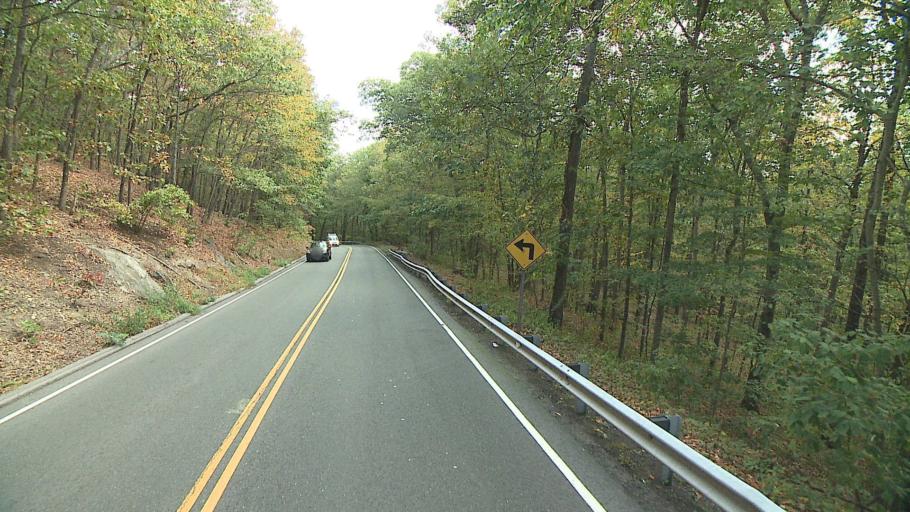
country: US
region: Connecticut
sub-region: New Haven County
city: Ansonia
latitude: 41.3548
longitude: -73.1028
